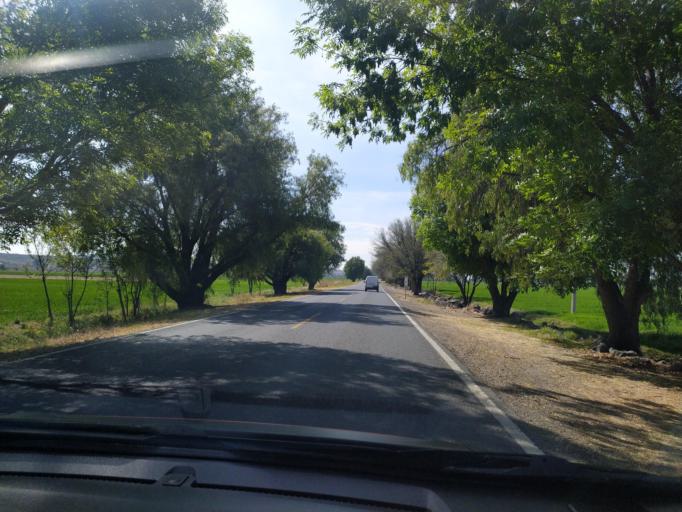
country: MX
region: Guanajuato
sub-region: San Francisco del Rincon
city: San Ignacio de Hidalgo
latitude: 20.9003
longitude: -101.8577
